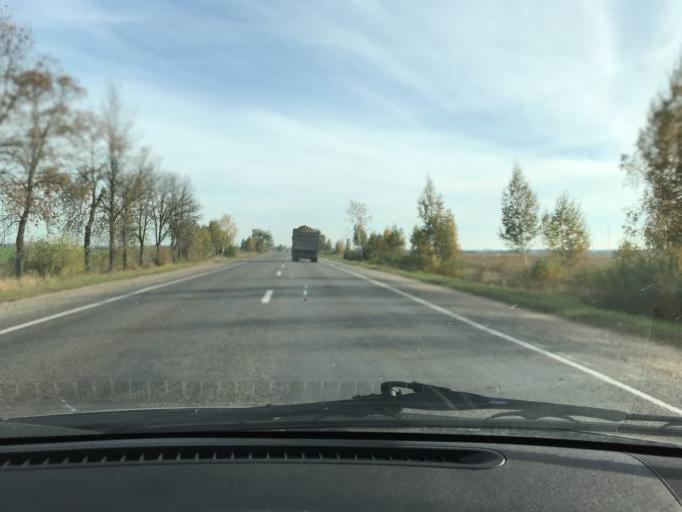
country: BY
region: Brest
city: Asnyezhytsy
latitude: 52.2127
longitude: 26.0447
